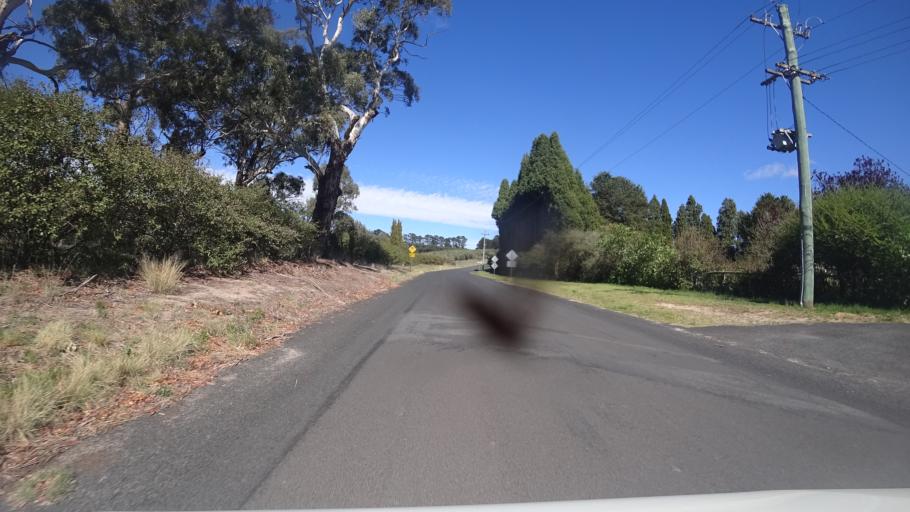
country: AU
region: New South Wales
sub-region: Lithgow
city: Bowenfels
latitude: -33.5168
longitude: 149.9931
